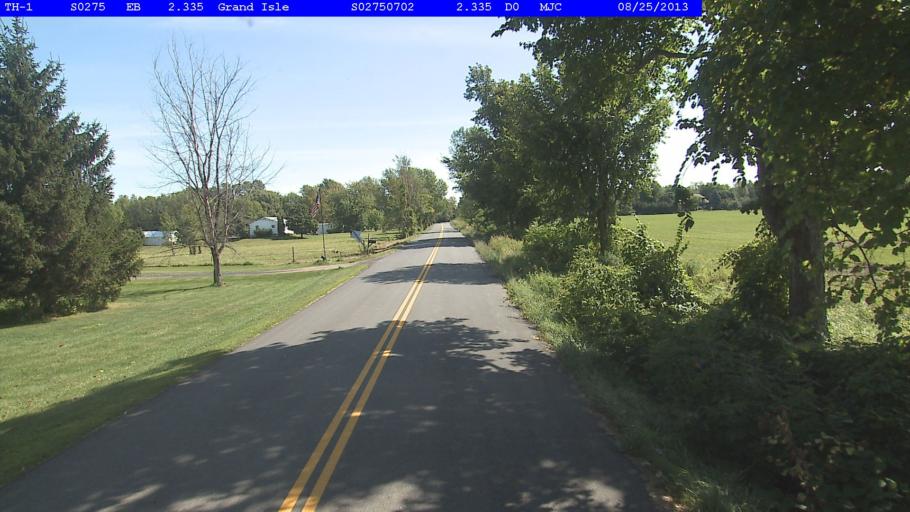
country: US
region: New York
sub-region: Clinton County
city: Cumberland Head
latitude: 44.7322
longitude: -73.3339
